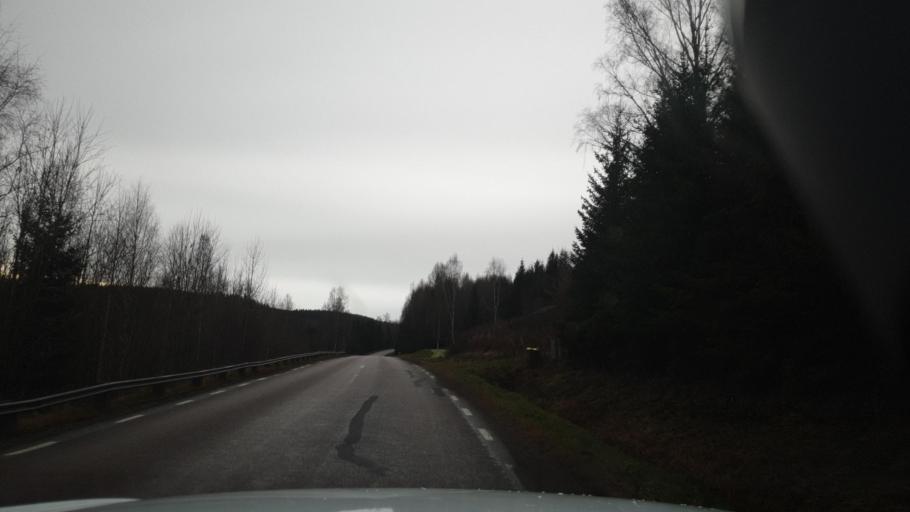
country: SE
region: Vaermland
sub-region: Arvika Kommun
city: Arvika
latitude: 59.7298
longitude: 12.7980
